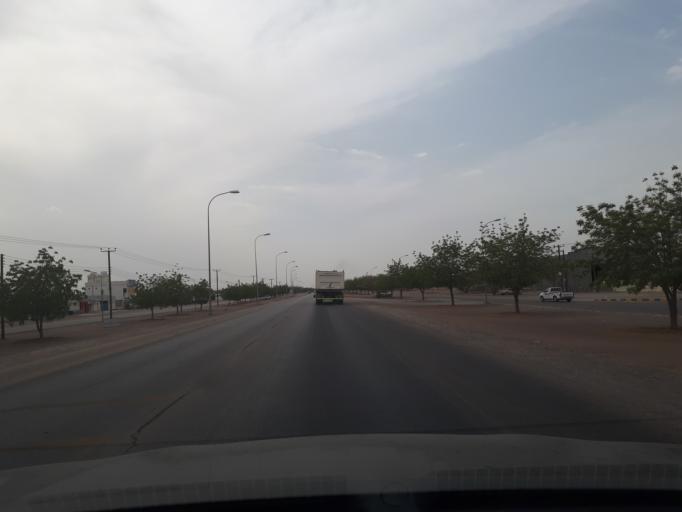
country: OM
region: Ash Sharqiyah
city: Badiyah
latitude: 22.4588
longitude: 58.8012
